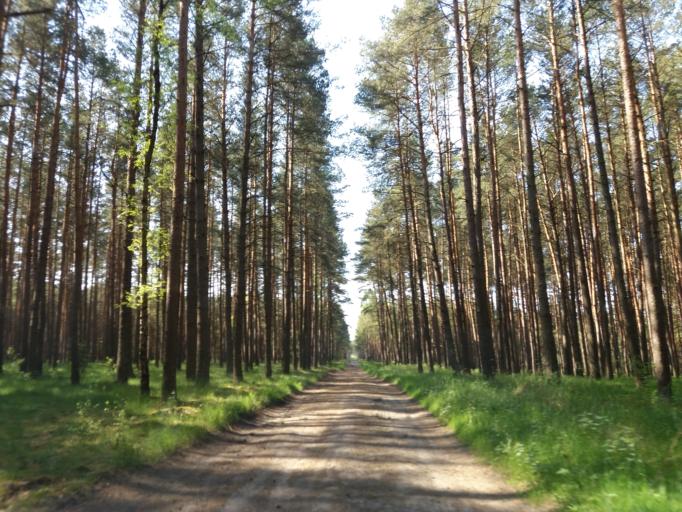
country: PL
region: West Pomeranian Voivodeship
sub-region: Powiat choszczenski
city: Bierzwnik
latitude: 53.1125
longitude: 15.6887
